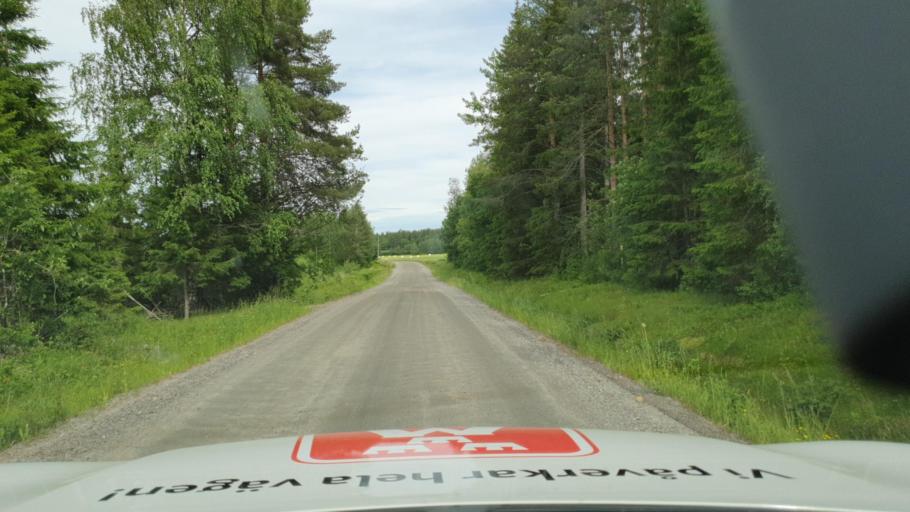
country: SE
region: Vaesterbotten
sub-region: Skelleftea Kommun
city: Viken
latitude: 64.5102
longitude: 20.9357
